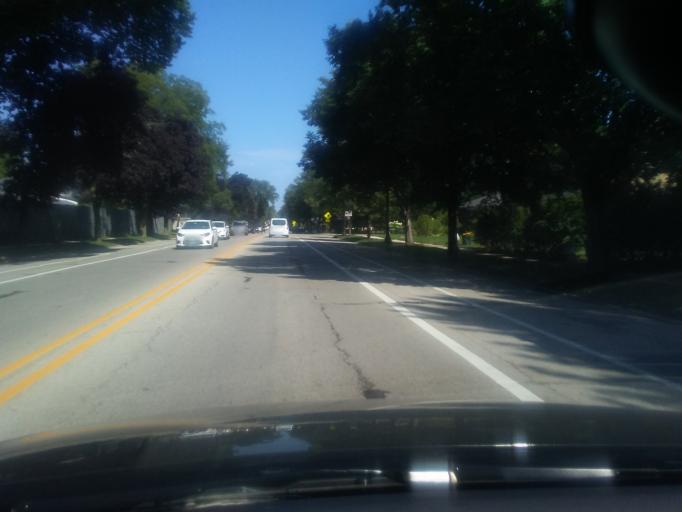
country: US
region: Illinois
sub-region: Cook County
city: Wilmette
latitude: 42.0646
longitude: -87.7253
